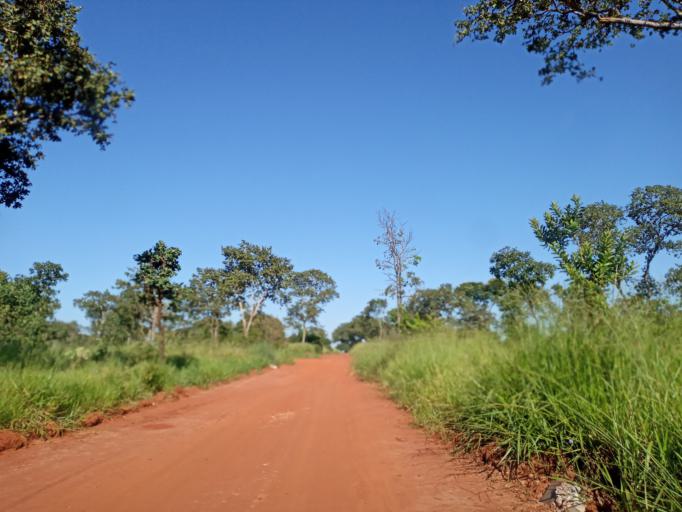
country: BR
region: Minas Gerais
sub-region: Ituiutaba
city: Ituiutaba
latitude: -18.9691
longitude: -49.4985
